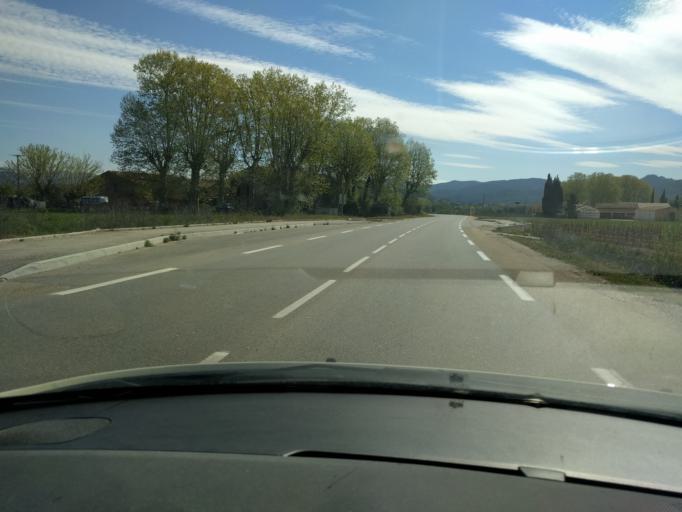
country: FR
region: Provence-Alpes-Cote d'Azur
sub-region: Departement du Var
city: Pierrefeu-du-Var
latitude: 43.2265
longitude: 6.1242
